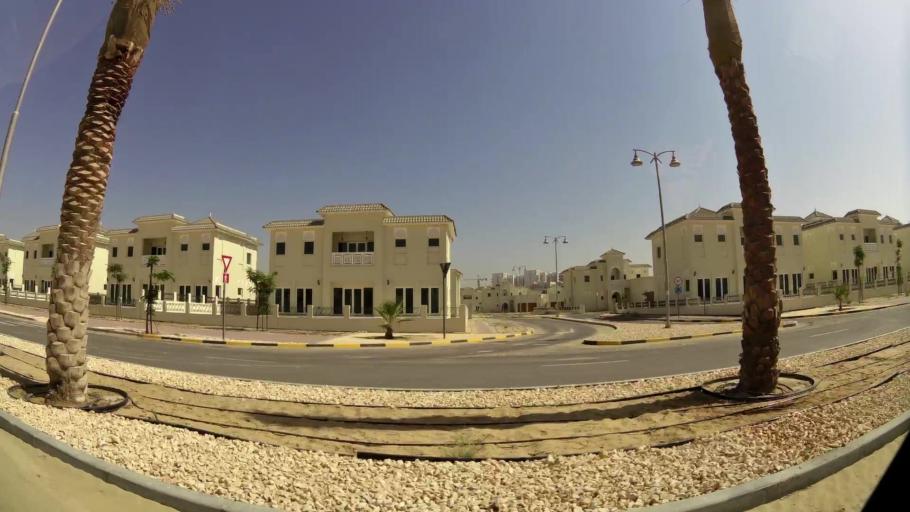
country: AE
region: Dubai
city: Dubai
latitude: 25.0264
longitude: 55.1486
